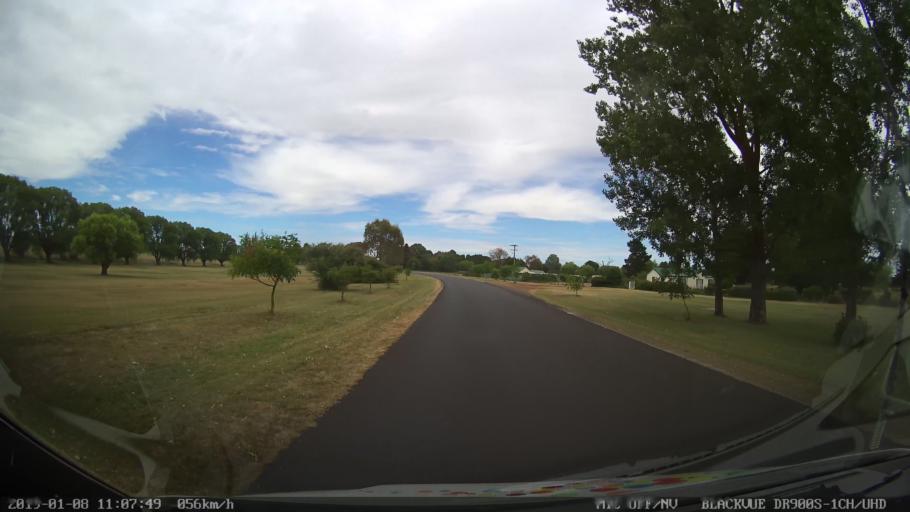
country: AU
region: New South Wales
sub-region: Guyra
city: Guyra
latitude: -30.2177
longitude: 151.6623
